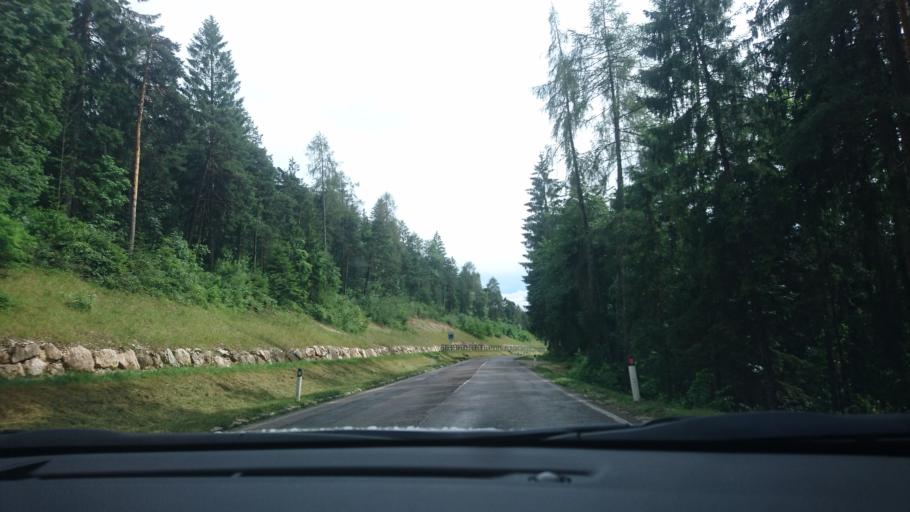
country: IT
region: Trentino-Alto Adige
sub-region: Provincia di Trento
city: Dambel
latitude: 46.3884
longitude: 11.0979
